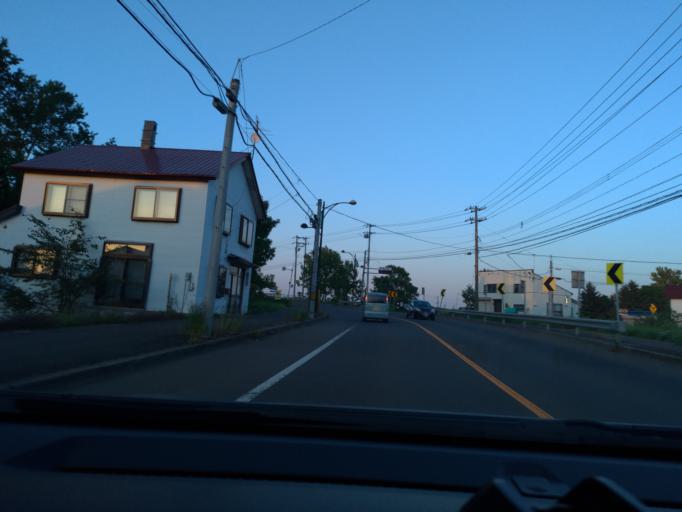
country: JP
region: Hokkaido
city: Iwamizawa
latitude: 43.3344
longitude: 141.6712
